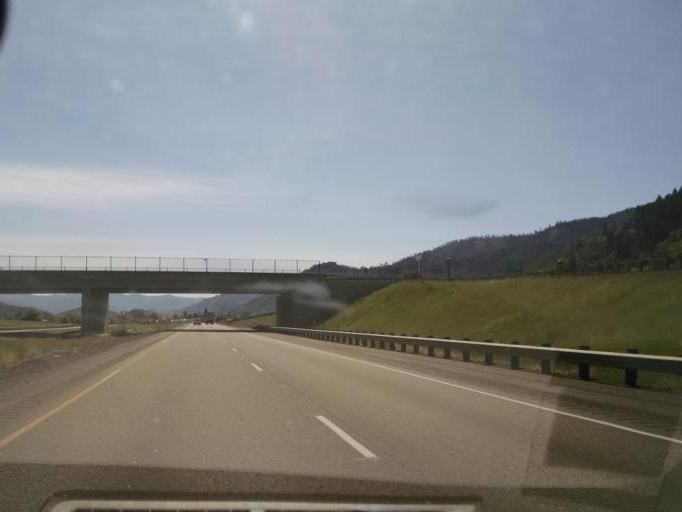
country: US
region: Oregon
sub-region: Douglas County
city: Myrtle Creek
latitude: 43.0072
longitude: -123.3069
